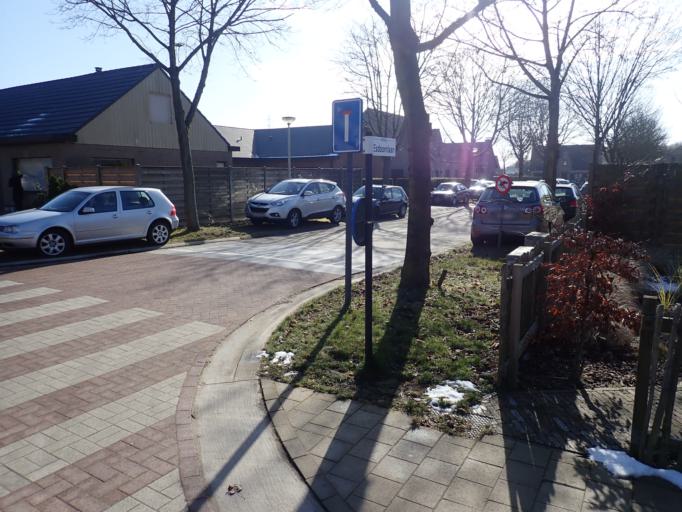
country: BE
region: Flanders
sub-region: Provincie Antwerpen
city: Lier
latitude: 51.1507
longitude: 4.6110
